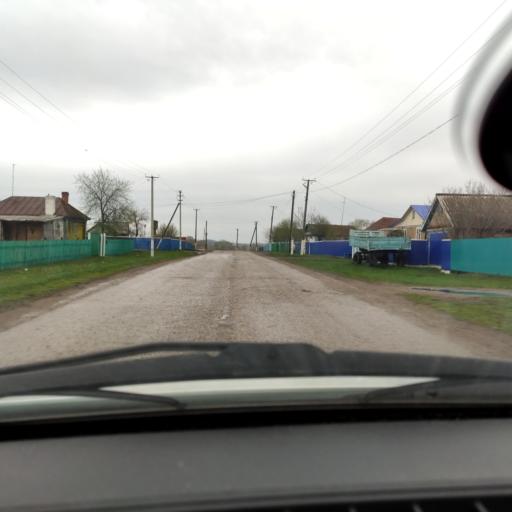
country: RU
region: Bashkortostan
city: Tolbazy
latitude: 54.1718
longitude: 55.9547
